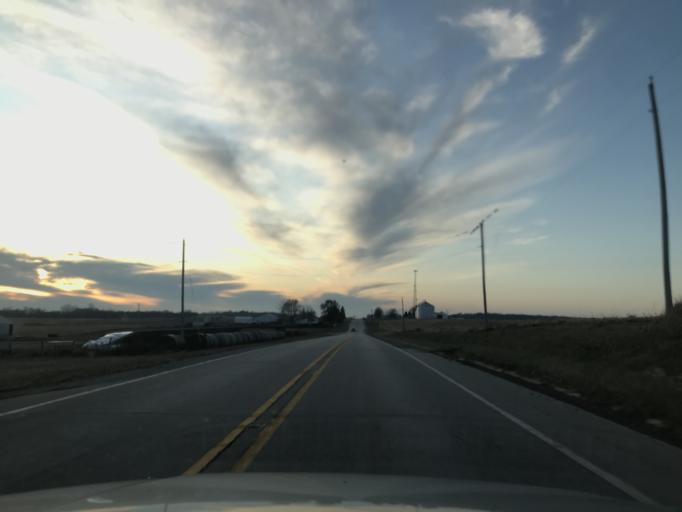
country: US
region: Illinois
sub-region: Henderson County
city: Oquawka
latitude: 41.0188
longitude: -90.8383
